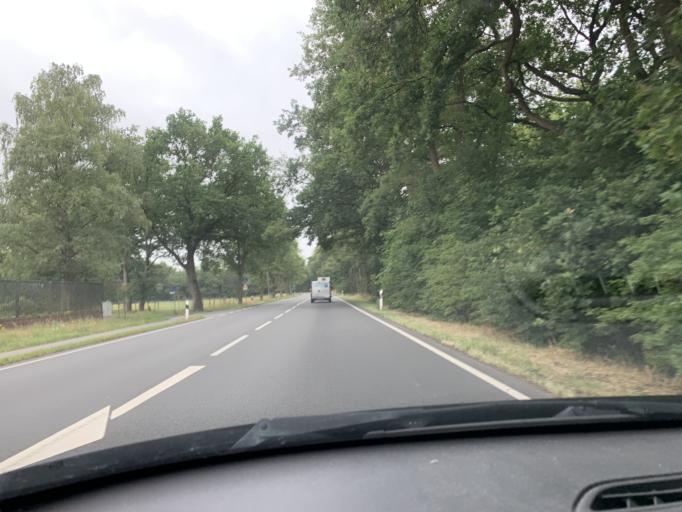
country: DE
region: Lower Saxony
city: Haselunne
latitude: 52.6668
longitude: 7.4832
